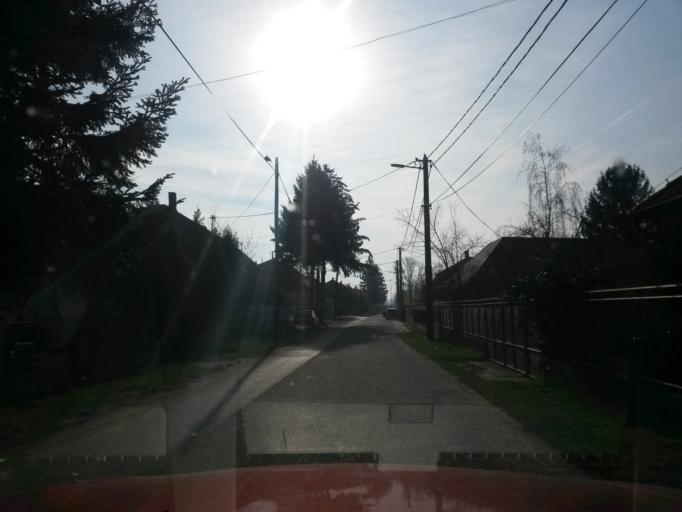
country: SK
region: Nitriansky
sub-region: Okres Komarno
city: Hurbanovo
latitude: 47.8834
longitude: 18.2028
